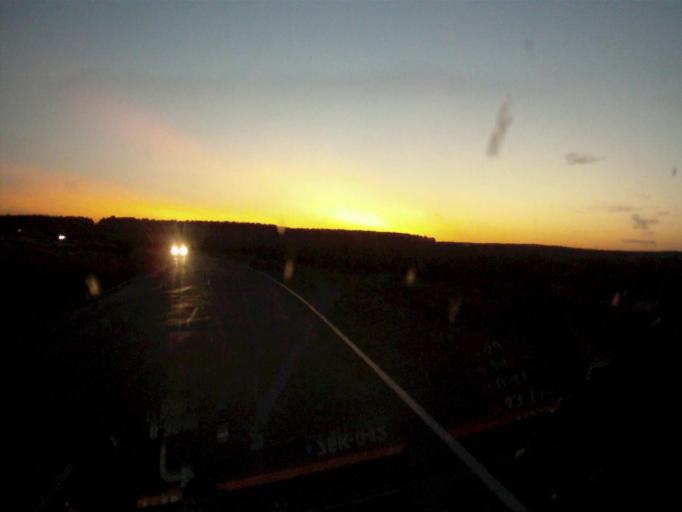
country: RU
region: Chelyabinsk
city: Timiryazevskiy
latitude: 55.2090
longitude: 60.7252
